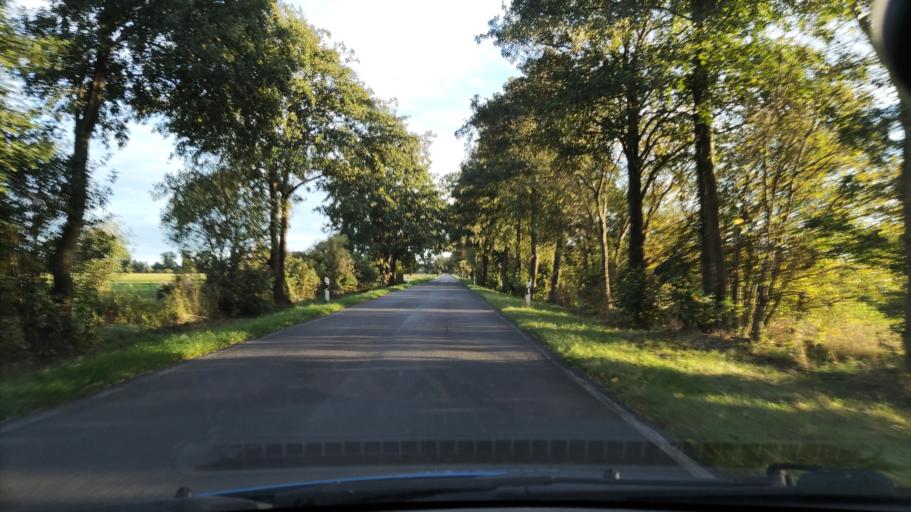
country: DE
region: Lower Saxony
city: Neu Darchau
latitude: 53.3633
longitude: 10.8646
